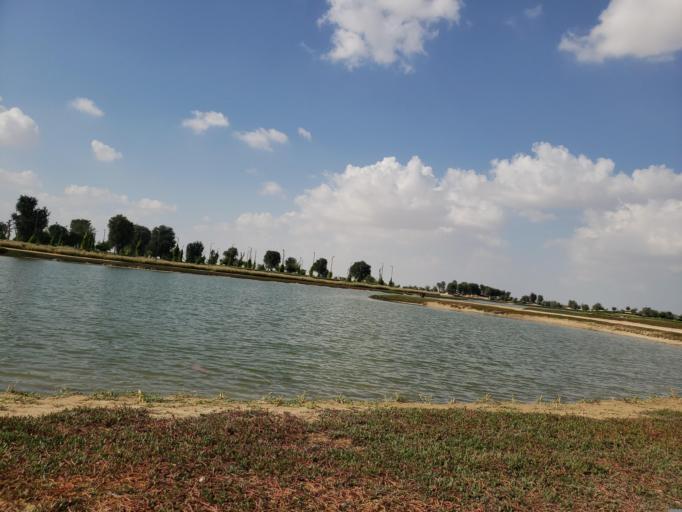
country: AE
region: Dubai
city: Dubai
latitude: 24.8559
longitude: 55.2499
